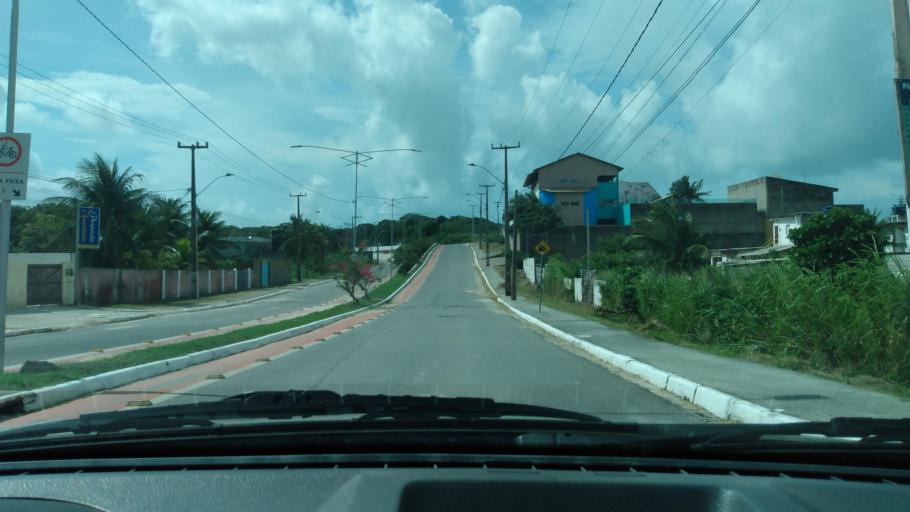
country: BR
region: Pernambuco
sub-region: Cabo De Santo Agostinho
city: Cabo
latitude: -8.3090
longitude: -34.9471
